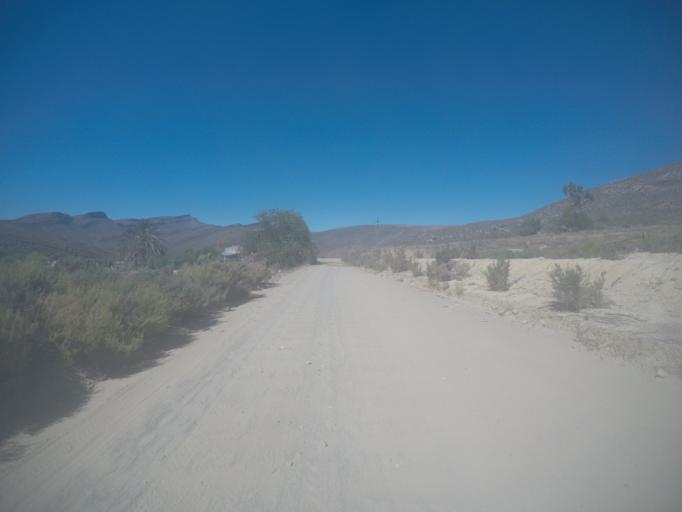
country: ZA
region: Western Cape
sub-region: West Coast District Municipality
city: Clanwilliam
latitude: -32.5503
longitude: 19.3608
